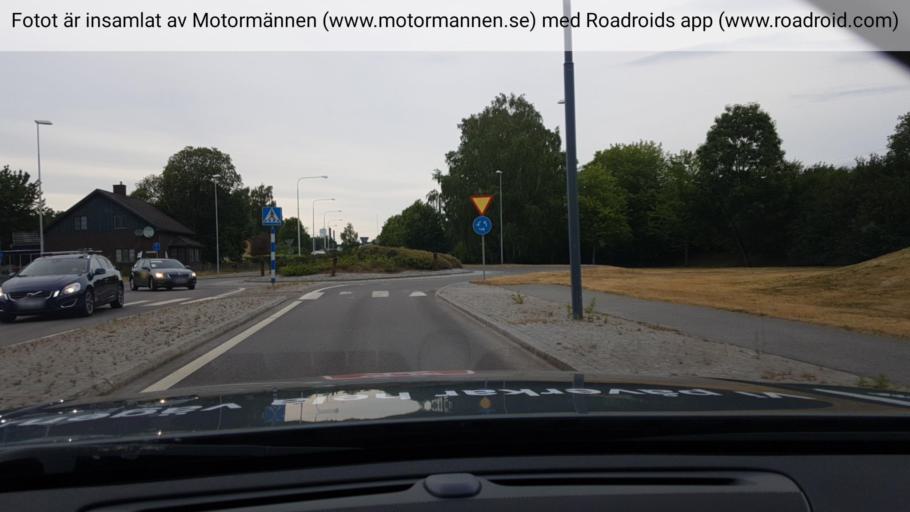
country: SE
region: OEstergoetland
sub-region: Motala Kommun
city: Motala
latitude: 58.5506
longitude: 15.0629
